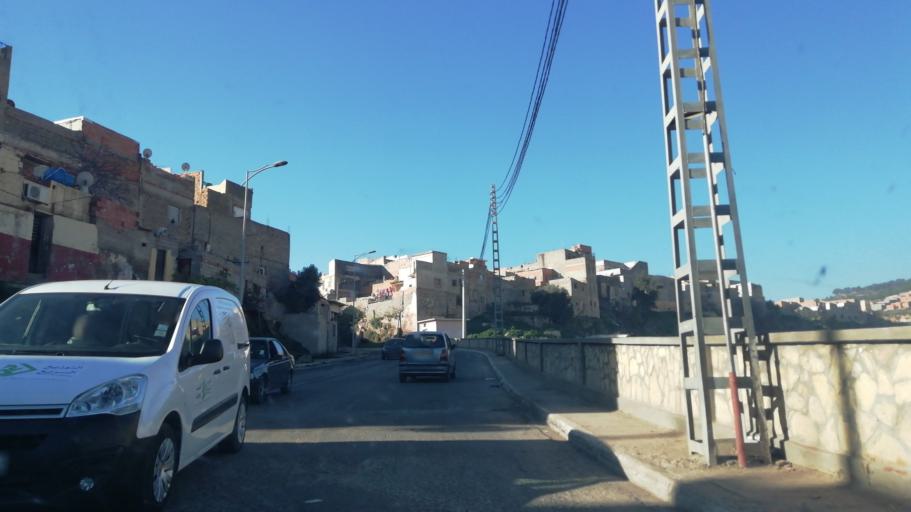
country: DZ
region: Oran
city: Oran
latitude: 35.6870
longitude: -0.6691
